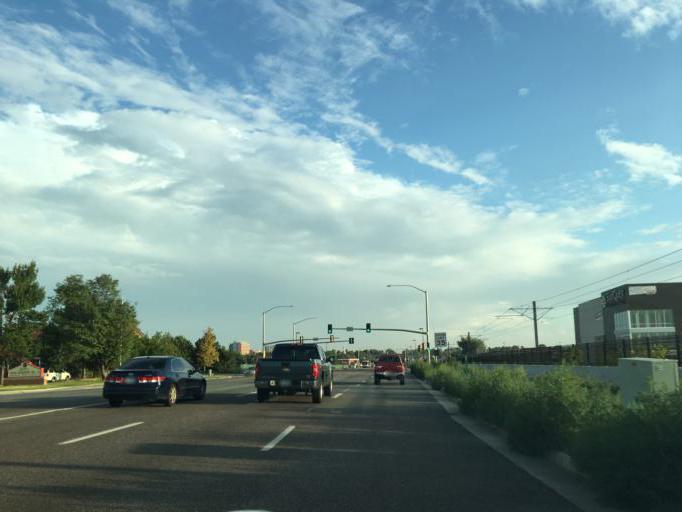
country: US
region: Colorado
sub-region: Adams County
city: Aurora
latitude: 39.7629
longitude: -104.8471
